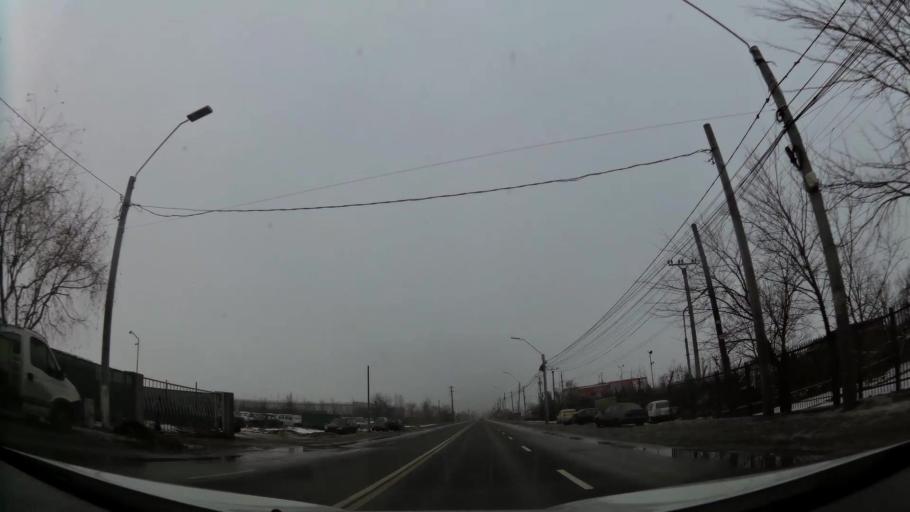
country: RO
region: Ilfov
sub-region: Comuna Magurele
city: Magurele
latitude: 44.3655
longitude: 26.0403
